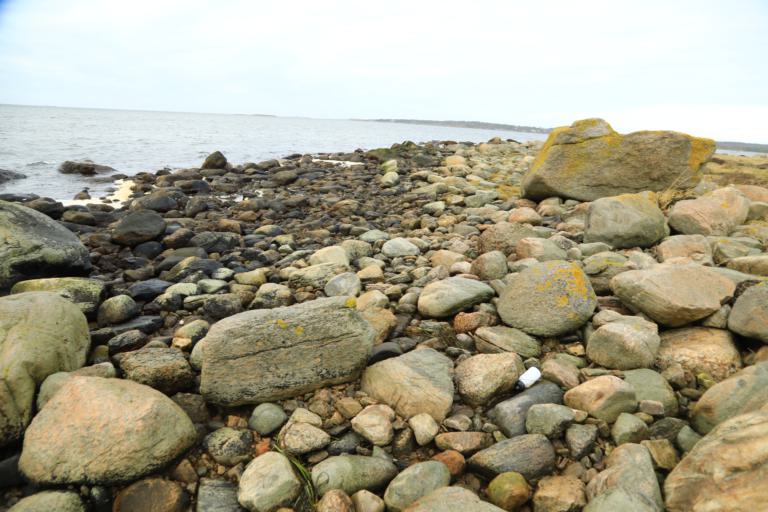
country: SE
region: Halland
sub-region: Varbergs Kommun
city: Varberg
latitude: 57.1739
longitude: 12.2013
